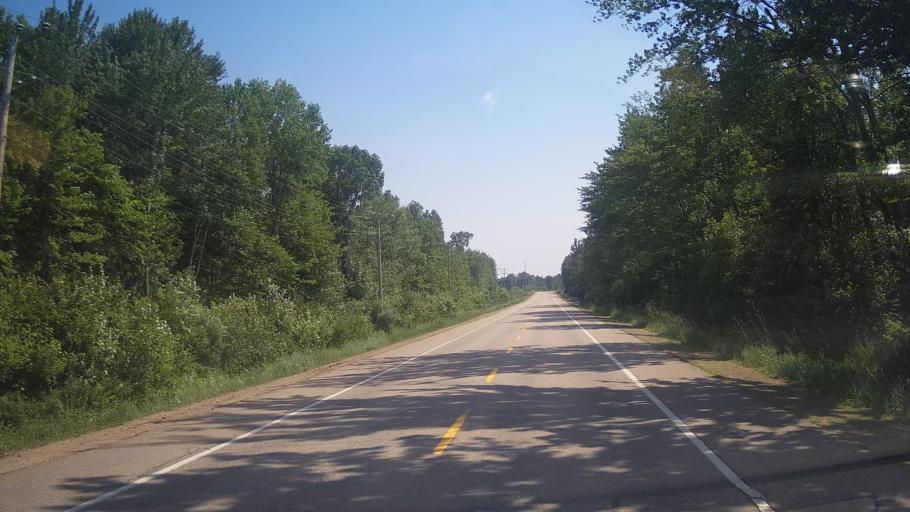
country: CA
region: Ontario
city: Pembroke
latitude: 45.8354
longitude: -77.0134
